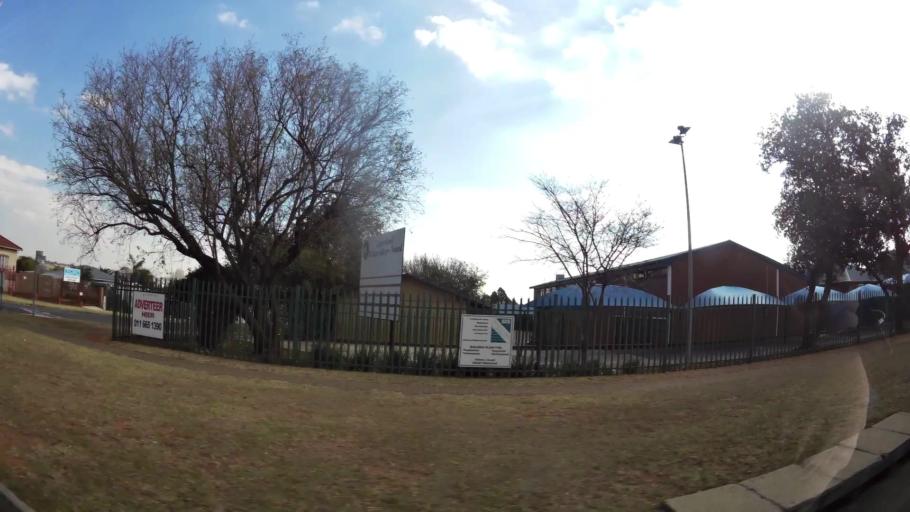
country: ZA
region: Gauteng
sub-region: West Rand District Municipality
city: Krugersdorp
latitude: -26.0906
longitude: 27.7711
